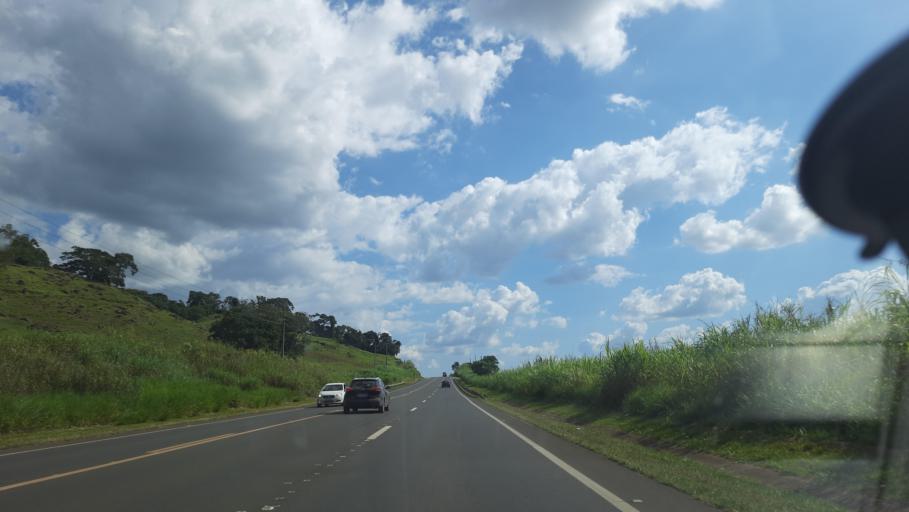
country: BR
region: Sao Paulo
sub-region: Sao Jose Do Rio Pardo
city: Sao Jose do Rio Pardo
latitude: -21.6540
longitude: -46.9132
